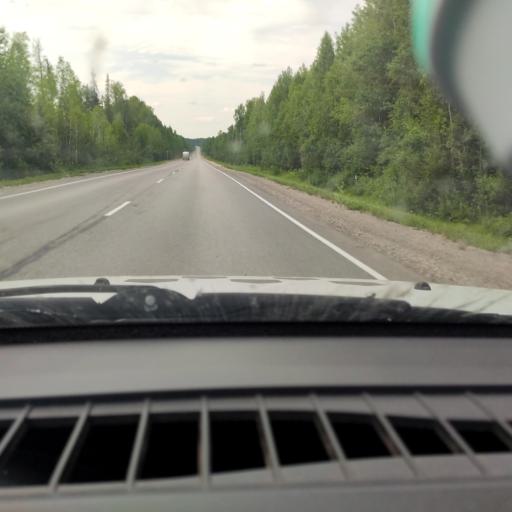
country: RU
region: Kirov
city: Chernaya Kholunitsa
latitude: 58.8359
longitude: 51.7553
